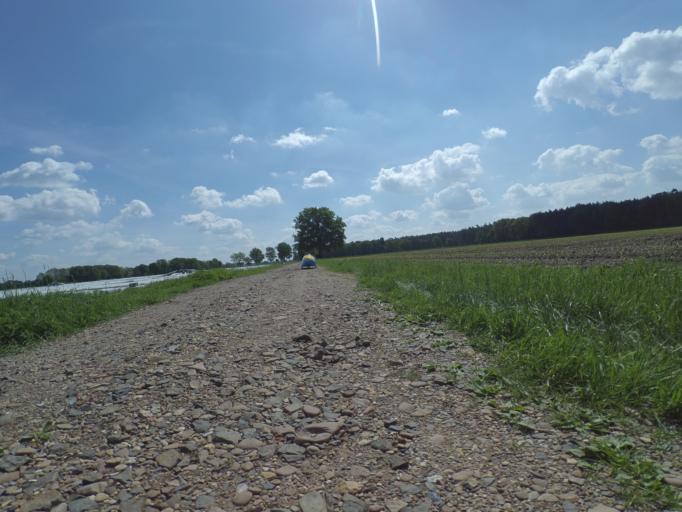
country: DE
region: Lower Saxony
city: Langlingen
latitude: 52.5437
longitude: 10.2571
